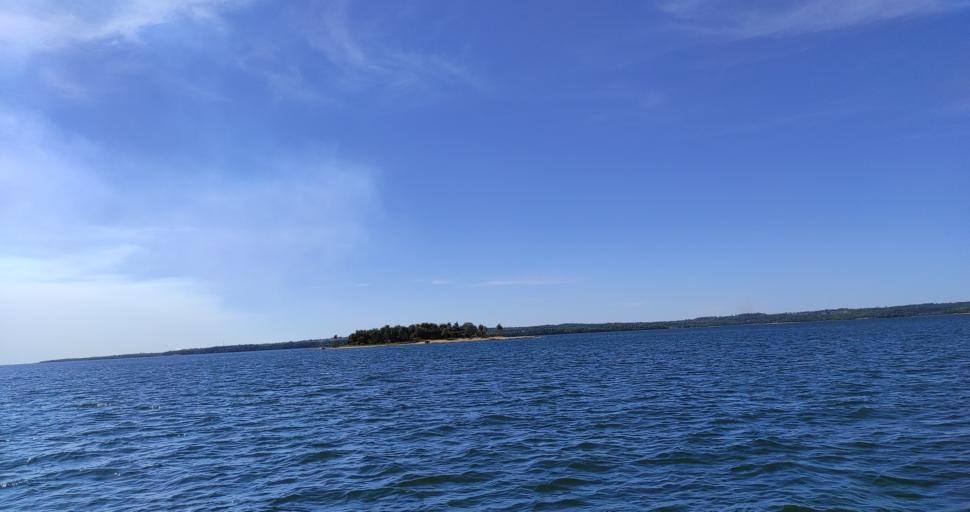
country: PY
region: Itapua
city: San Juan del Parana
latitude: -27.3437
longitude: -55.9472
